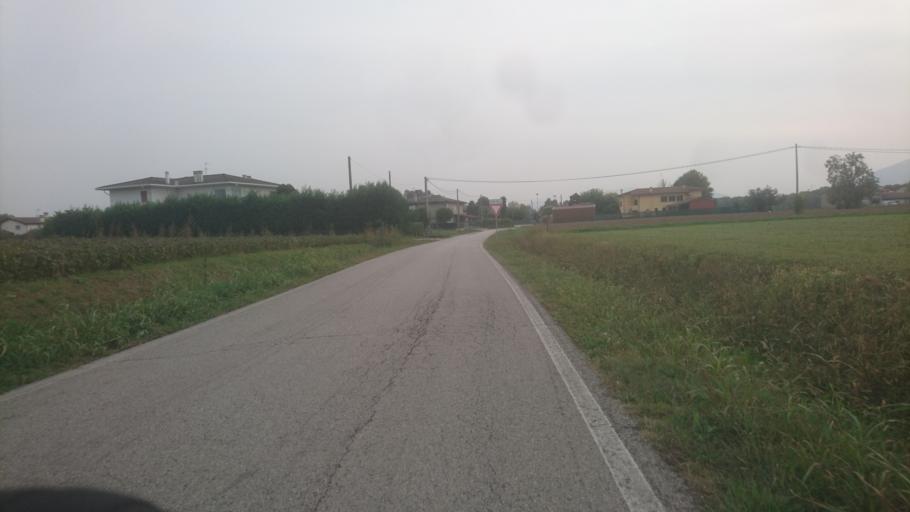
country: IT
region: Veneto
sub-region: Provincia di Padova
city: Saccolongo
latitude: 45.4136
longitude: 11.7292
